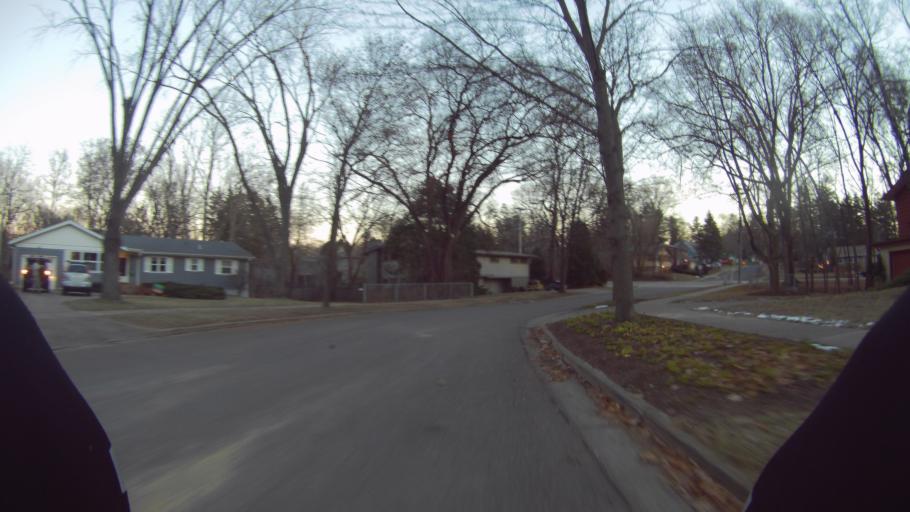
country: US
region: Wisconsin
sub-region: Dane County
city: Shorewood Hills
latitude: 43.0615
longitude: -89.4563
